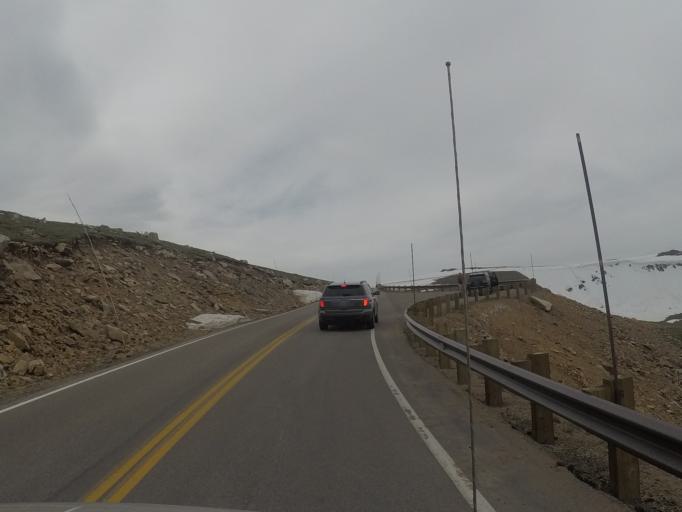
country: US
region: Montana
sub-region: Carbon County
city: Red Lodge
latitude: 44.9892
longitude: -109.4267
